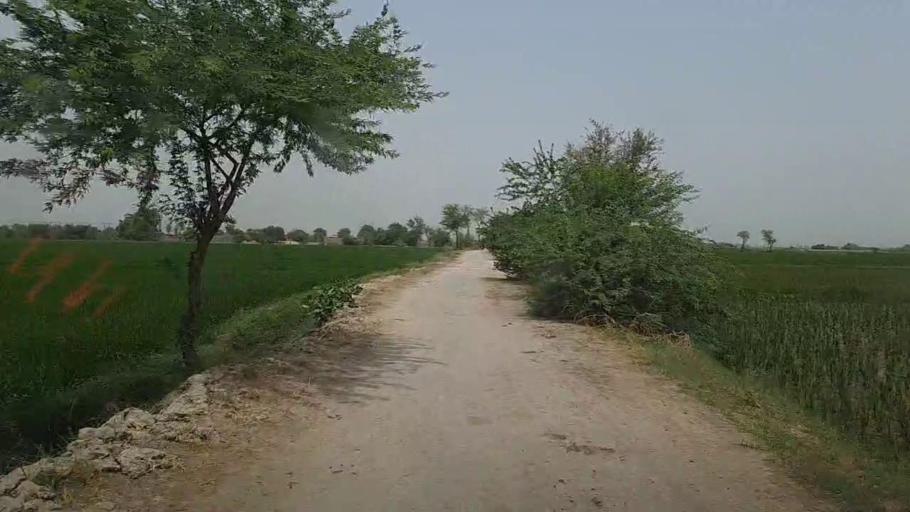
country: PK
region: Sindh
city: Sita Road
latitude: 27.0636
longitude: 67.8489
